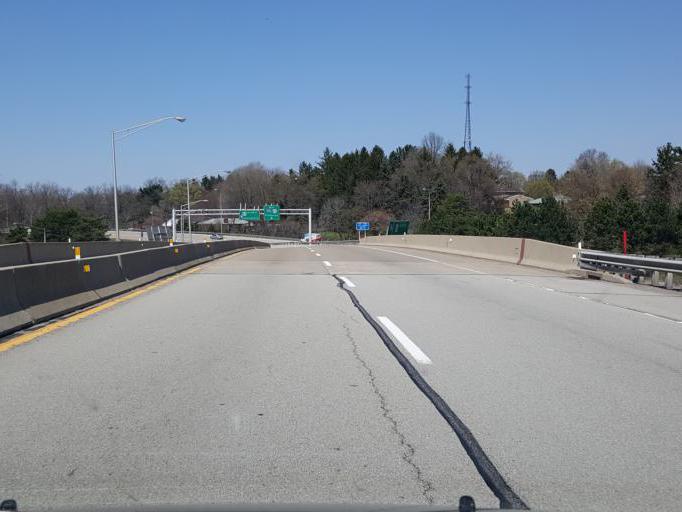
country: US
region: Pennsylvania
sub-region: Allegheny County
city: Monroeville
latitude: 40.4379
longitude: -79.7546
